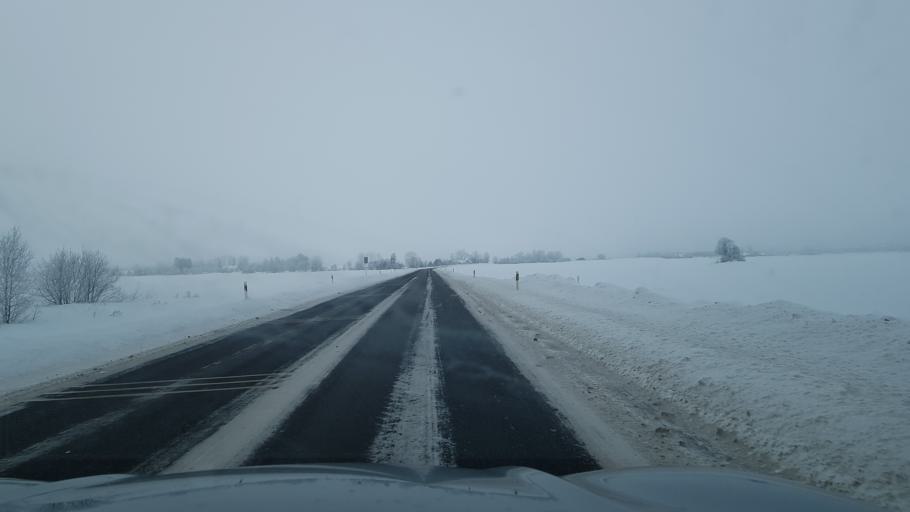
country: EE
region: Ida-Virumaa
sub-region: Johvi vald
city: Johvi
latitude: 59.3106
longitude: 27.3927
